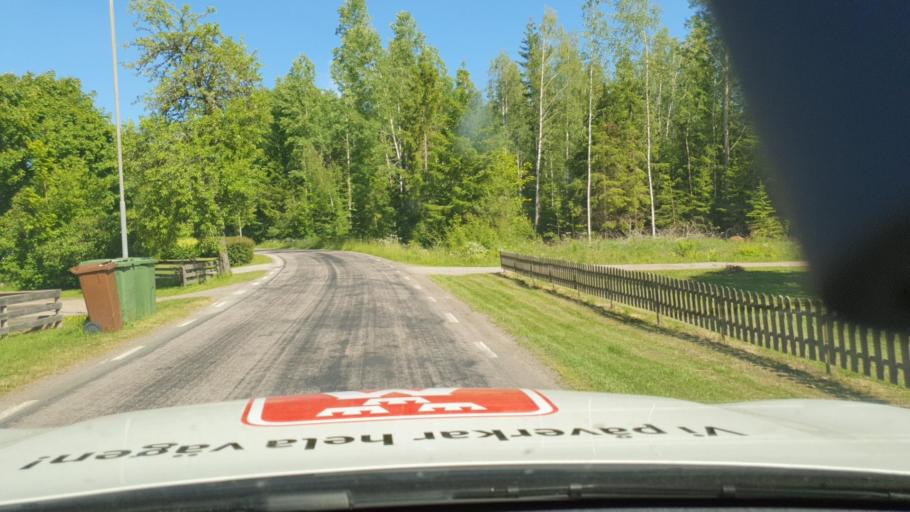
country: SE
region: Vaestra Goetaland
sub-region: Skovde Kommun
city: Skultorp
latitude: 58.3289
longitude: 13.9221
